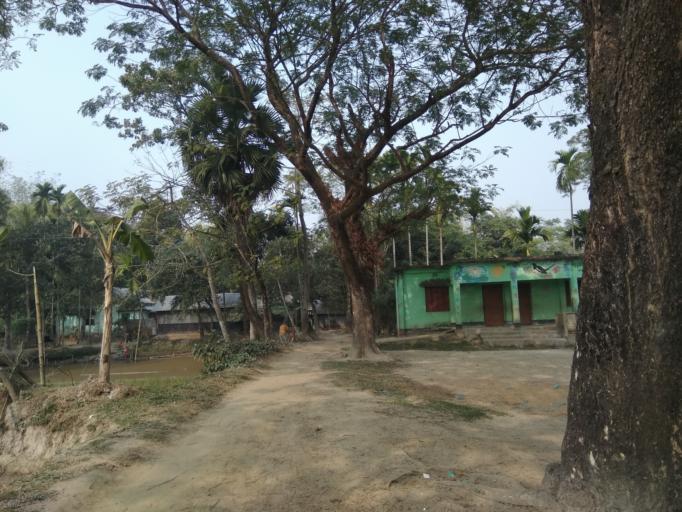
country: BD
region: Dhaka
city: Netrakona
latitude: 24.8935
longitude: 90.6647
